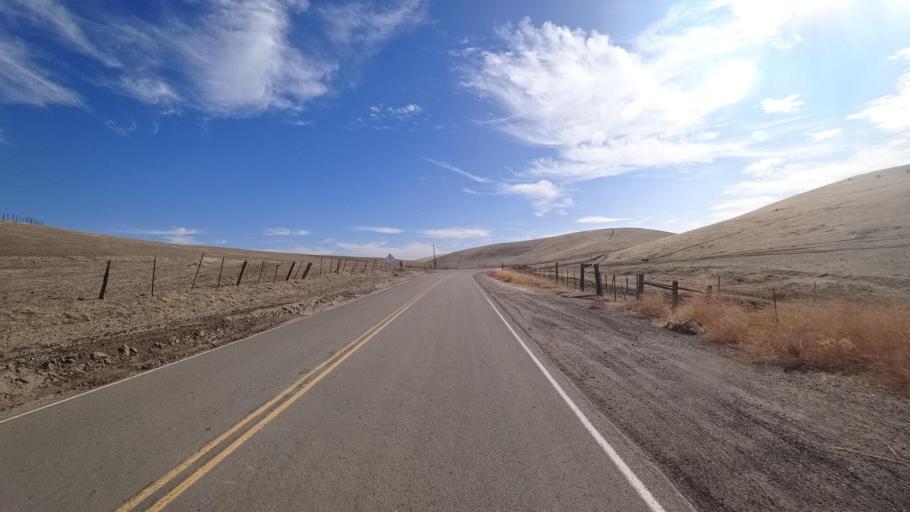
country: US
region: California
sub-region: Kern County
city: Oildale
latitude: 35.6023
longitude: -118.9493
